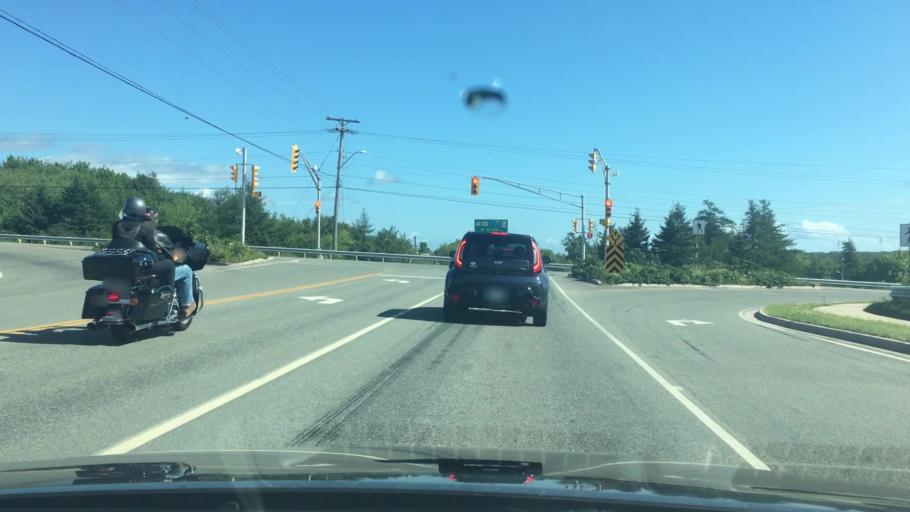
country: CA
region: Nova Scotia
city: Port Hawkesbury
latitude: 45.6122
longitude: -61.3456
